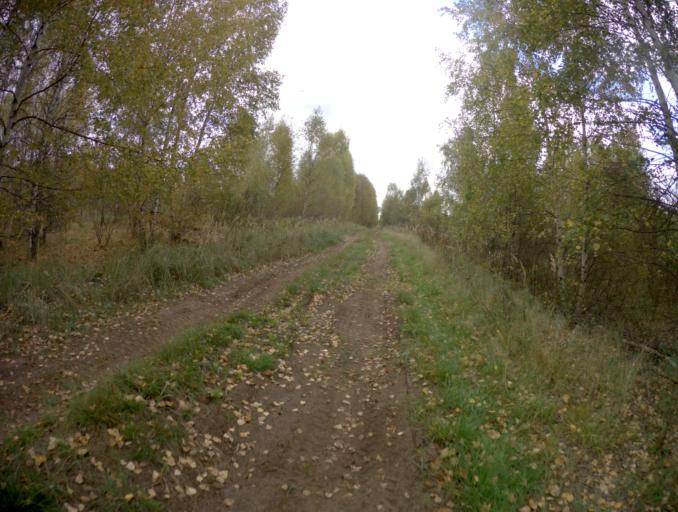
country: RU
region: Vladimir
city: Urshel'skiy
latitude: 55.7711
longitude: 40.1354
